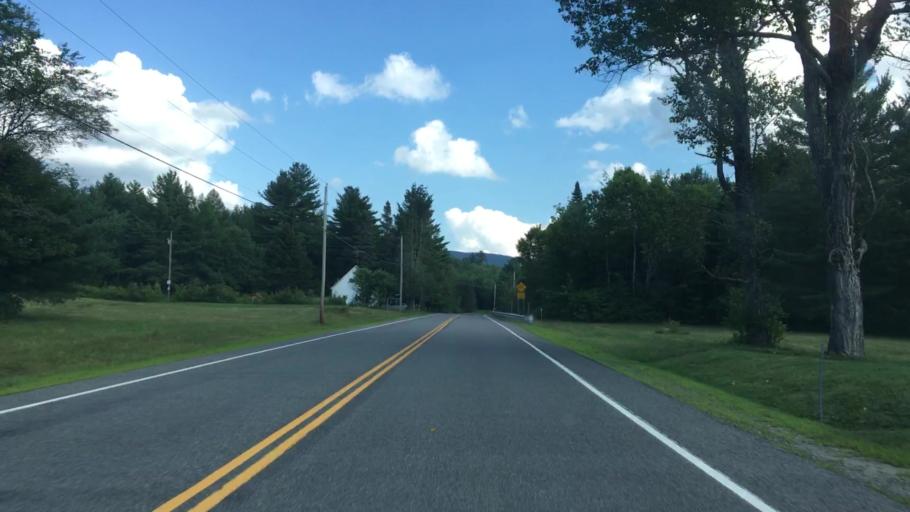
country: US
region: New Hampshire
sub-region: Grafton County
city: Woodstock
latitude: 44.0947
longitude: -71.8297
